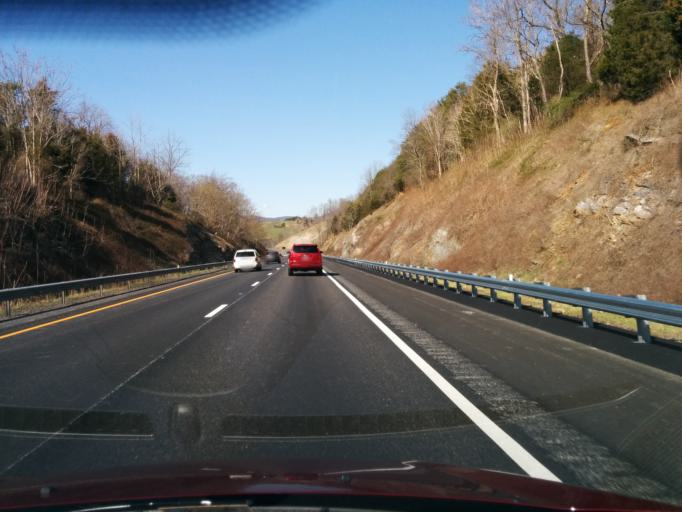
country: US
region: Virginia
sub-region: Rockbridge County
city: East Lexington
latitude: 37.7706
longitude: -79.4029
